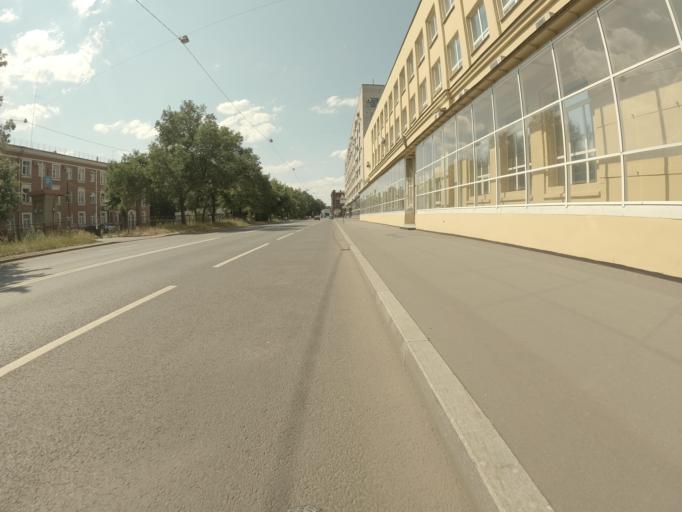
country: RU
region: St.-Petersburg
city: Vasyl'evsky Ostrov
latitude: 59.9110
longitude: 30.2549
